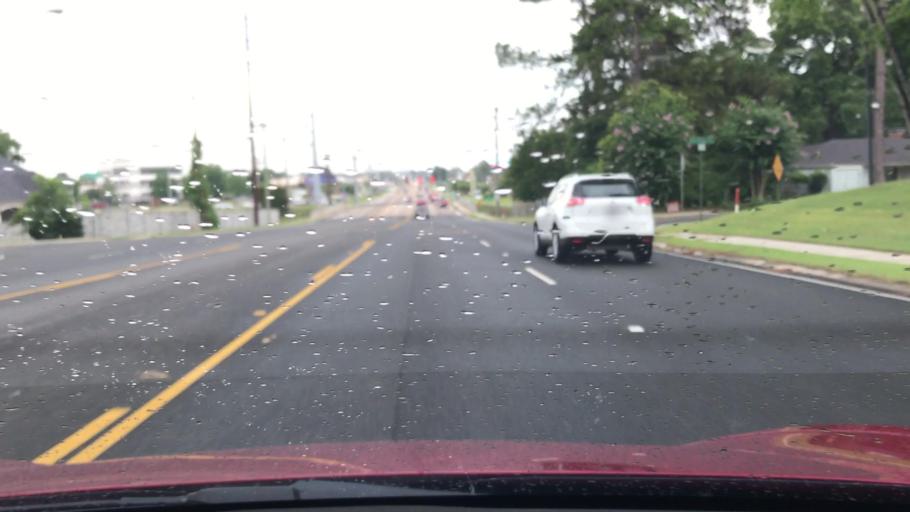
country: US
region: Louisiana
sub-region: Bossier Parish
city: Bossier City
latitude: 32.4434
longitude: -93.7323
